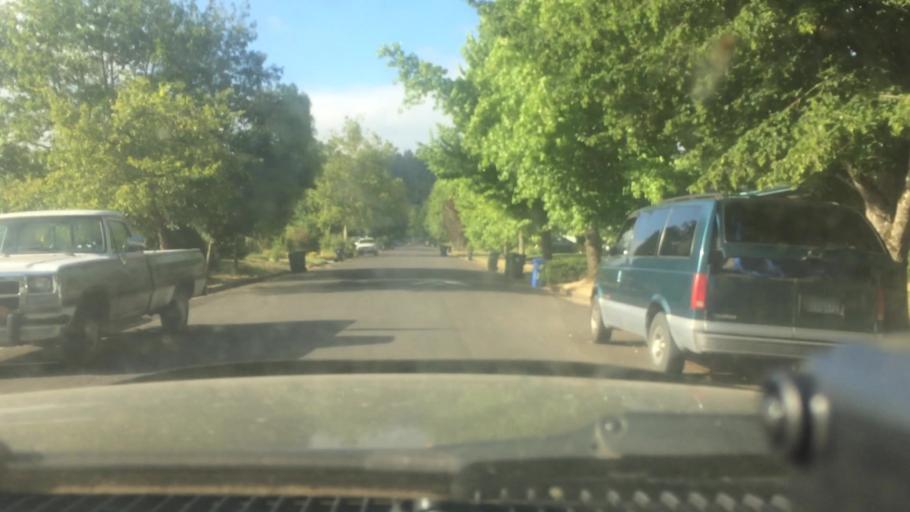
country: US
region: Oregon
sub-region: Lane County
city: Eugene
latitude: 44.0324
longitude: -123.1111
